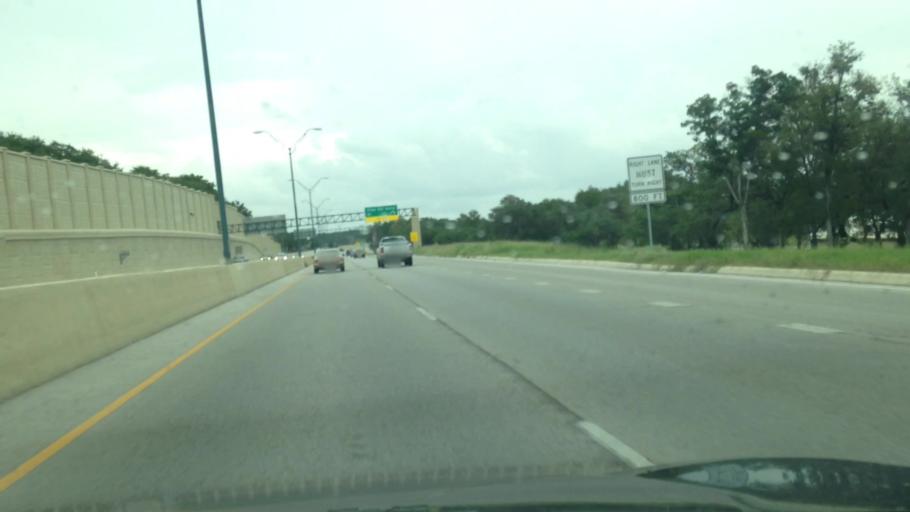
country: US
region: Texas
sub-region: Bexar County
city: Castle Hills
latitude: 29.5595
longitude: -98.5130
